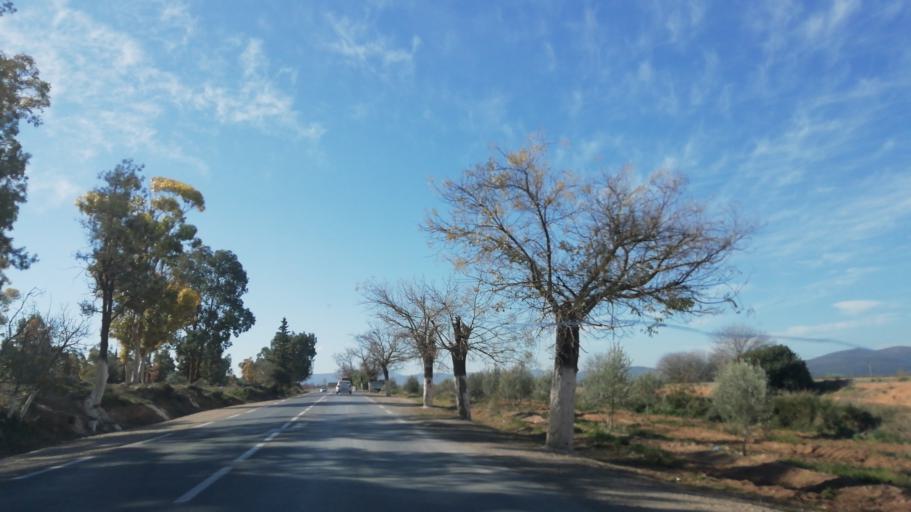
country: DZ
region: Tlemcen
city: Ouled Mimoun
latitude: 34.8969
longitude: -1.0561
